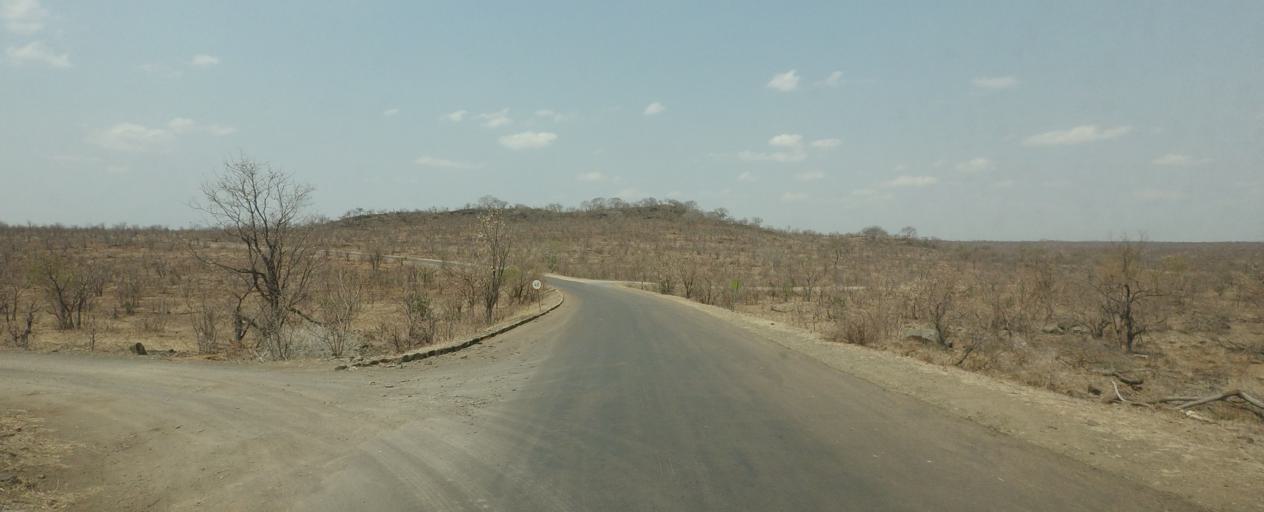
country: ZA
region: Limpopo
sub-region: Mopani District Municipality
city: Phalaborwa
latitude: -23.5217
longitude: 31.3992
